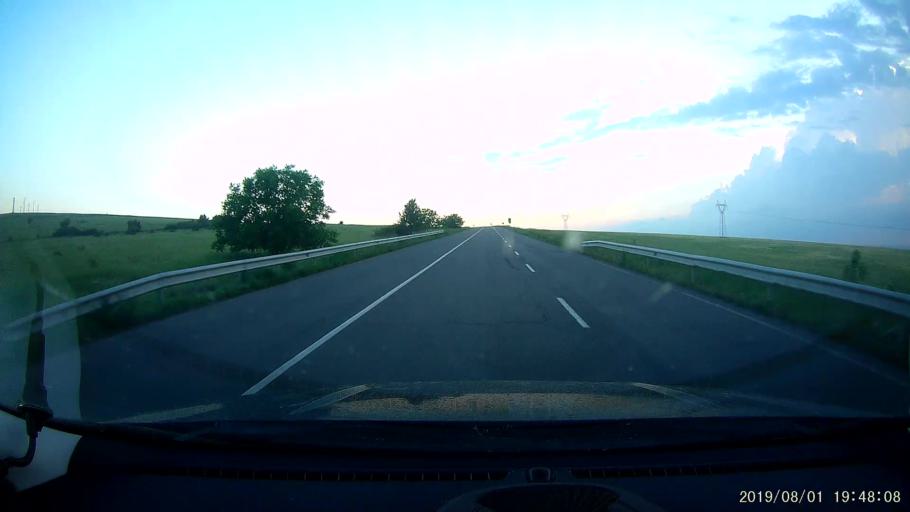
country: BG
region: Burgas
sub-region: Obshtina Karnobat
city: Karnobat
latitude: 42.6411
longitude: 26.9549
